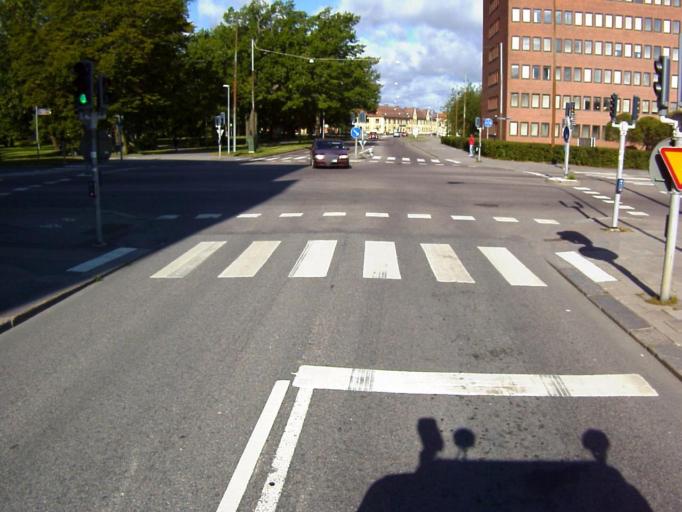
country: SE
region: Soedermanland
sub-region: Eskilstuna Kommun
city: Eskilstuna
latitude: 59.3723
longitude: 16.5082
